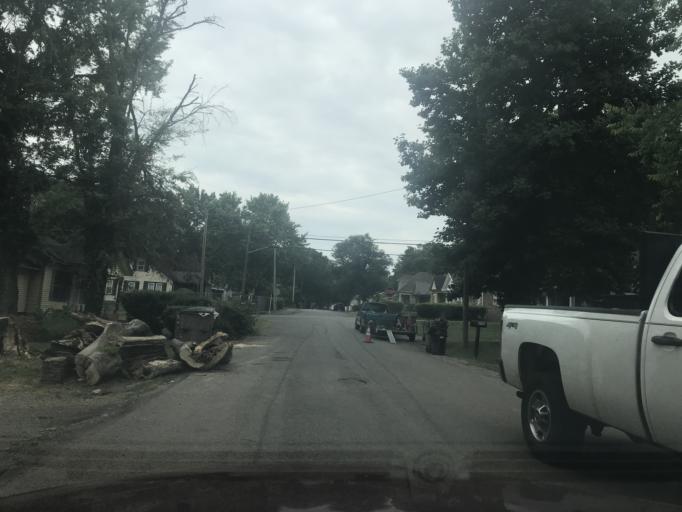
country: US
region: Tennessee
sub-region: Davidson County
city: Nashville
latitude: 36.1812
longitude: -86.8139
